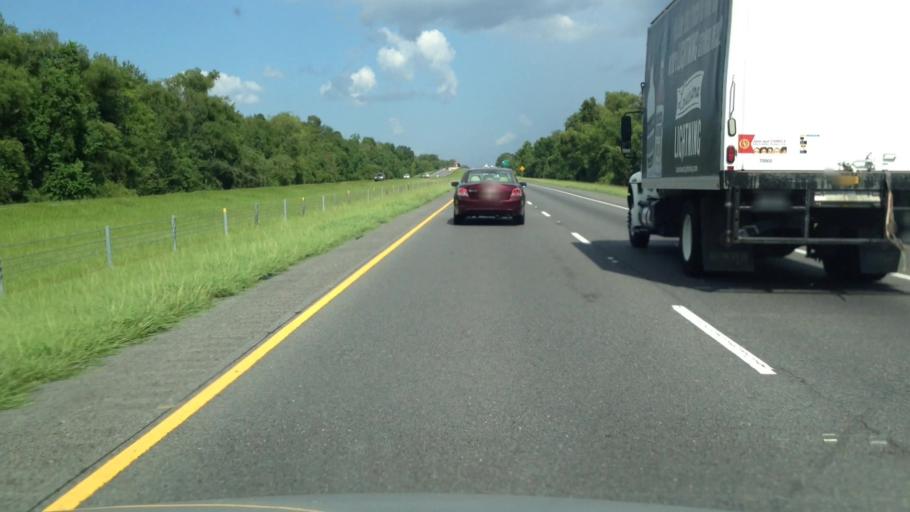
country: US
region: Louisiana
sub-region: Saint James Parish
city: Grand Point
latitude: 30.1332
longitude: -90.7252
